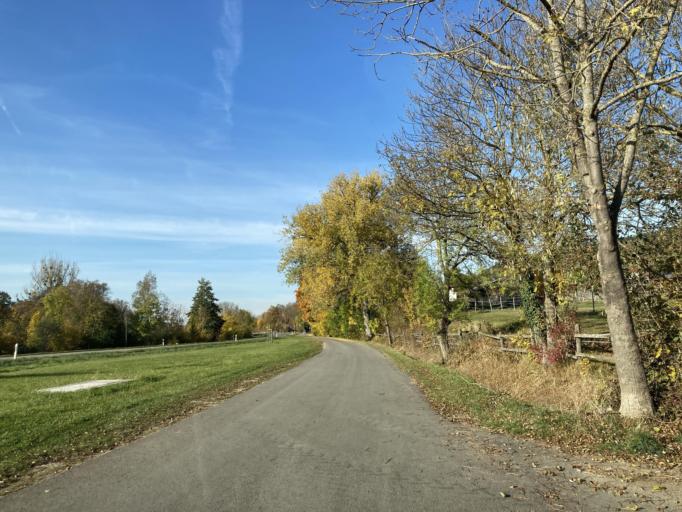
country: DE
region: Baden-Wuerttemberg
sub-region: Tuebingen Region
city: Mossingen
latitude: 48.3905
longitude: 9.1007
